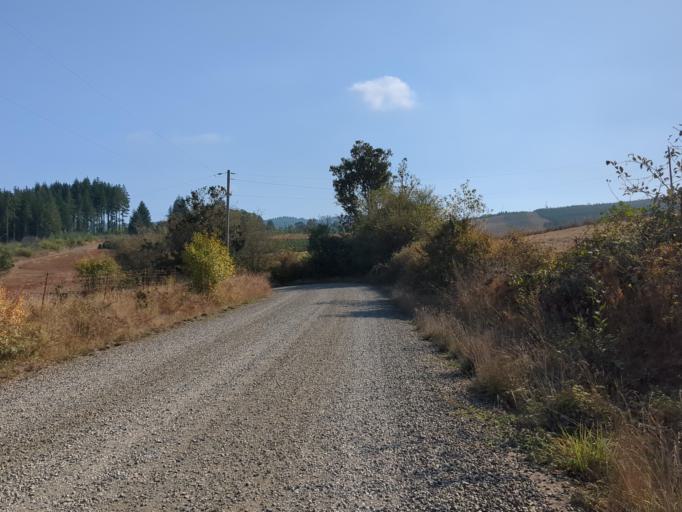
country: US
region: Oregon
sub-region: Lane County
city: Junction City
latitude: 44.2961
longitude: -123.3640
